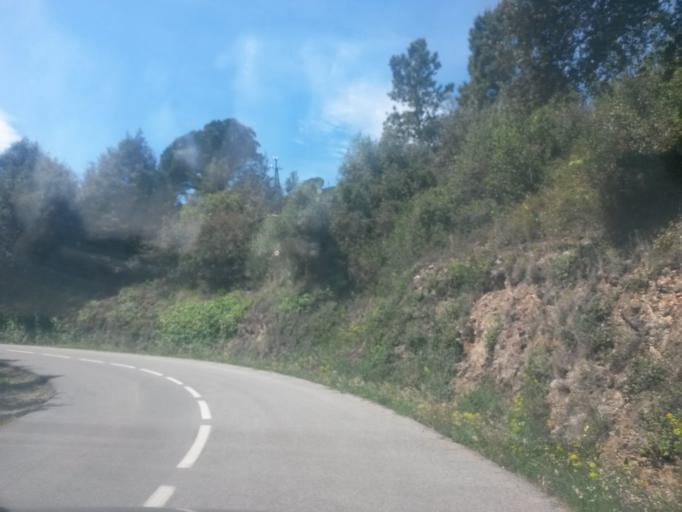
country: ES
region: Catalonia
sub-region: Provincia de Girona
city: Cassa de la Selva
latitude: 41.9157
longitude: 2.9092
